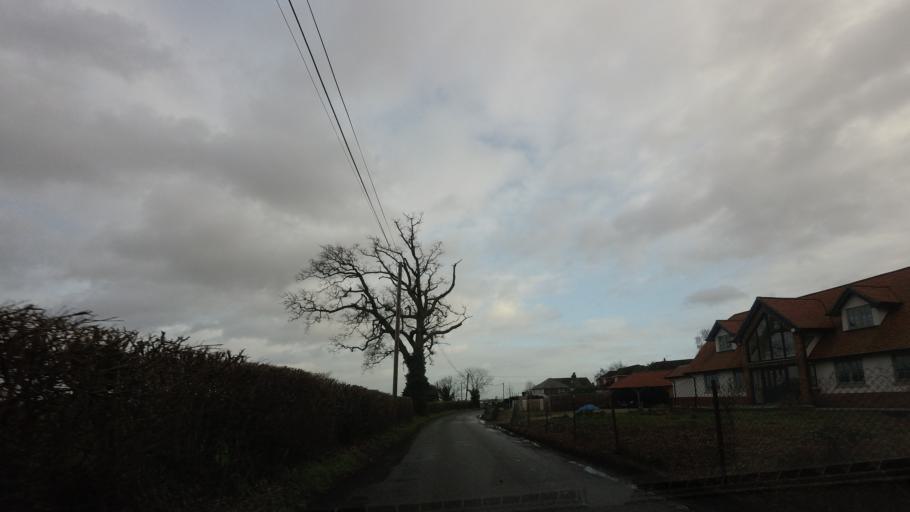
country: GB
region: England
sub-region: Kent
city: Hadlow
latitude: 51.2255
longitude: 0.3101
